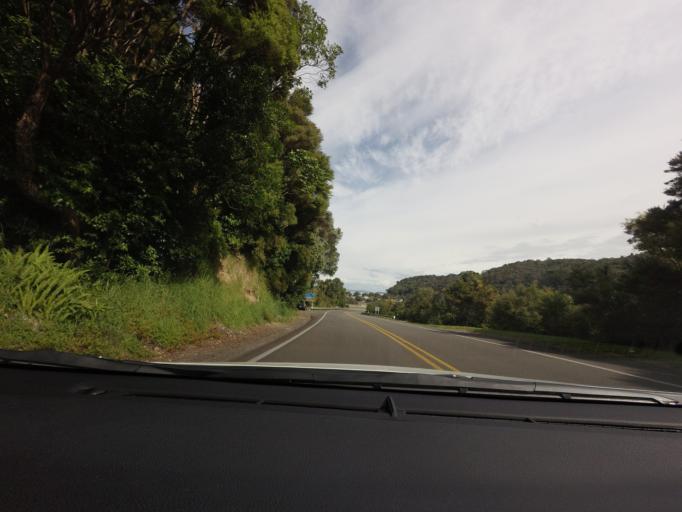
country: NZ
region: Auckland
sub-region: Auckland
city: Warkworth
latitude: -36.5395
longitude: 174.7051
